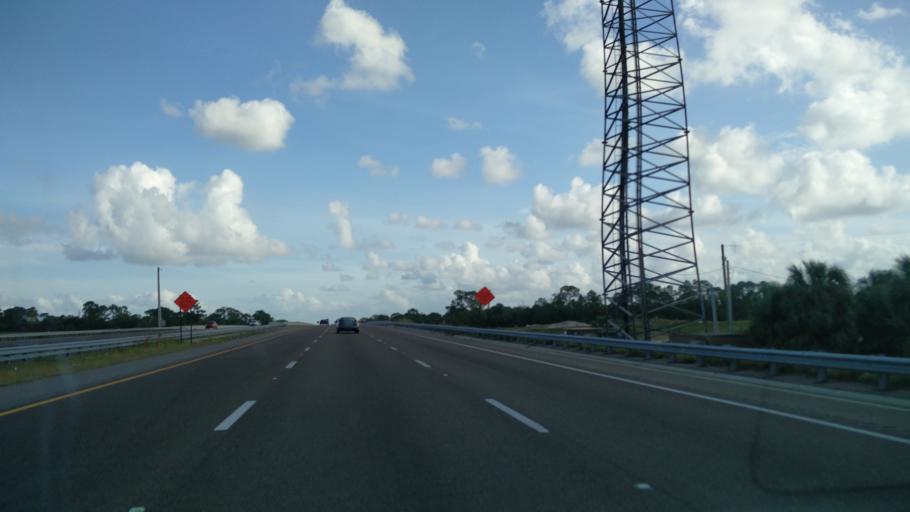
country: US
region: Florida
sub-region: Indian River County
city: Roseland
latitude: 27.8287
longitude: -80.5607
